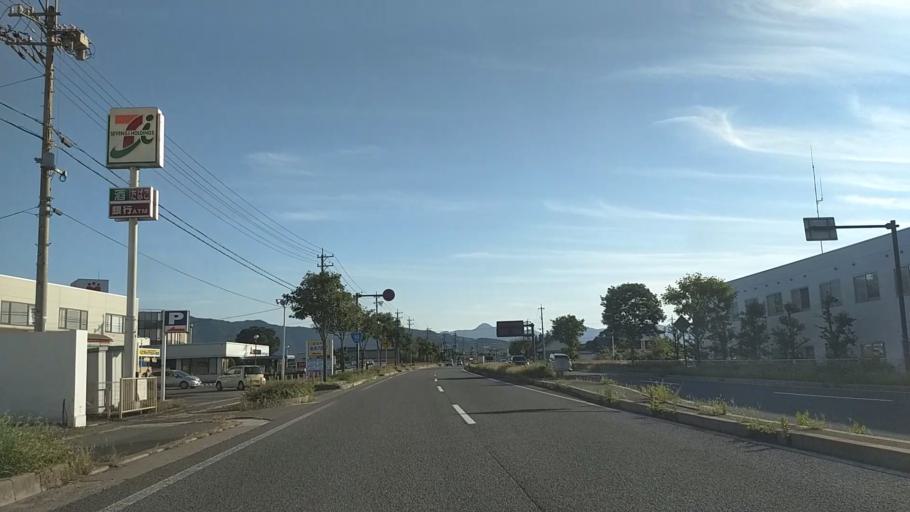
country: JP
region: Nagano
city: Nagano-shi
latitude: 36.6013
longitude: 138.1939
